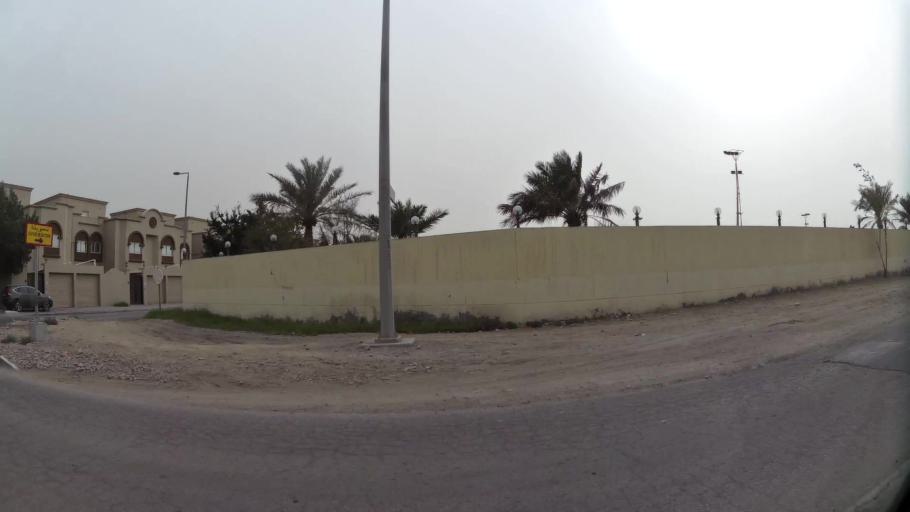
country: QA
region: Baladiyat ad Dawhah
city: Doha
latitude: 25.2478
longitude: 51.5019
